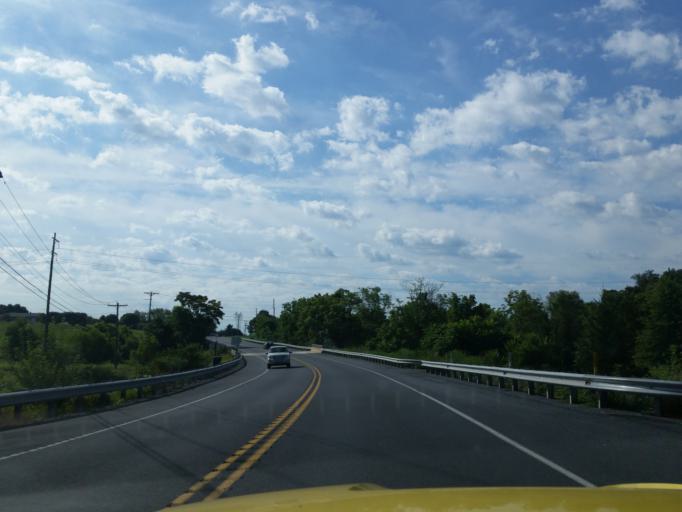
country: US
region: Pennsylvania
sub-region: Lebanon County
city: Fredericksburg
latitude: 40.4378
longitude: -76.4290
